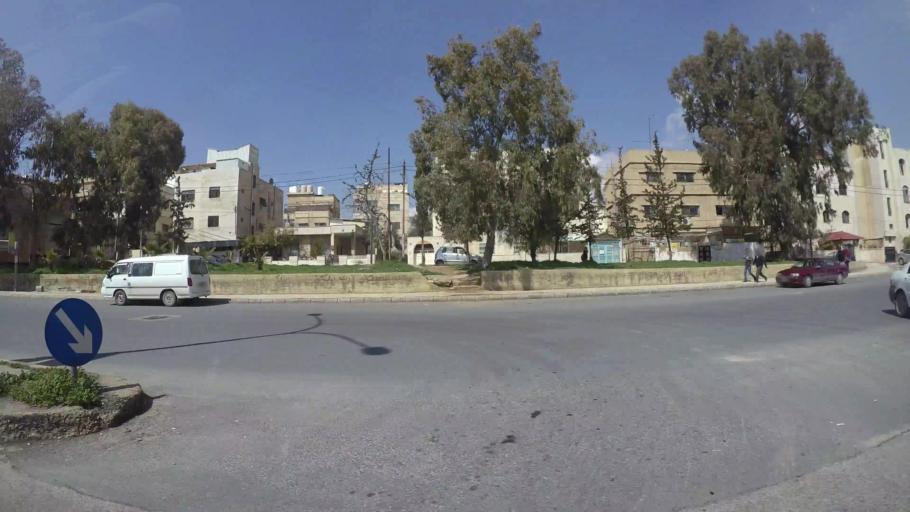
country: JO
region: Amman
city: Al Bunayyat ash Shamaliyah
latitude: 31.9291
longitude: 35.9088
